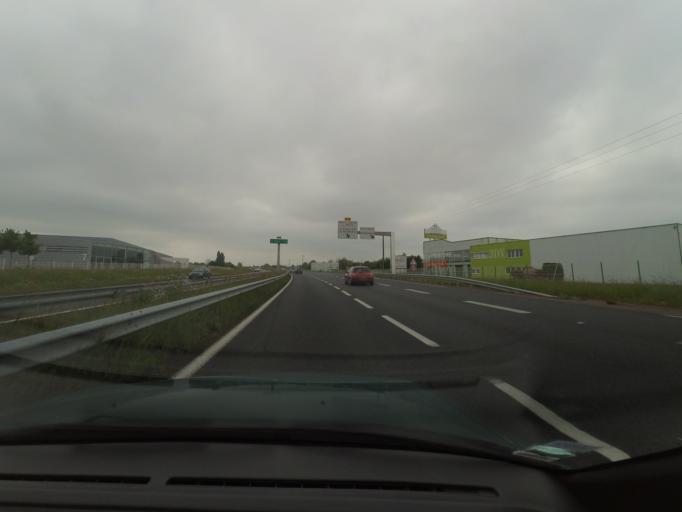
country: FR
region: Pays de la Loire
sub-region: Departement de la Vendee
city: Mouilleron-le-Captif
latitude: 46.7346
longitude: -1.4324
